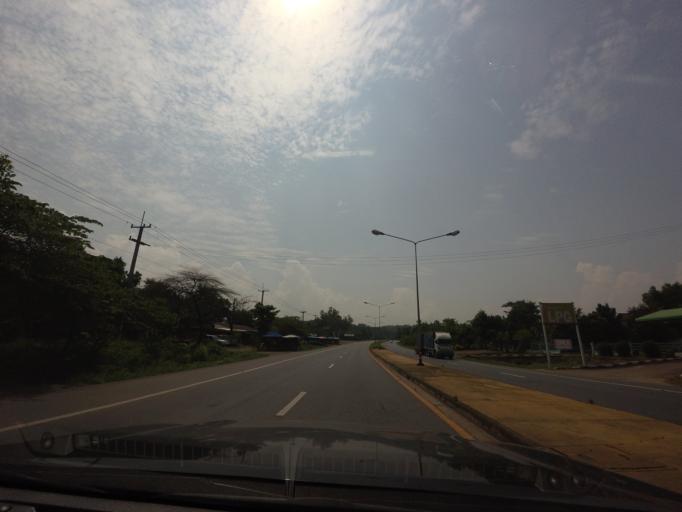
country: TH
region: Phrae
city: Den Chai
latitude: 17.9556
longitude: 100.0681
